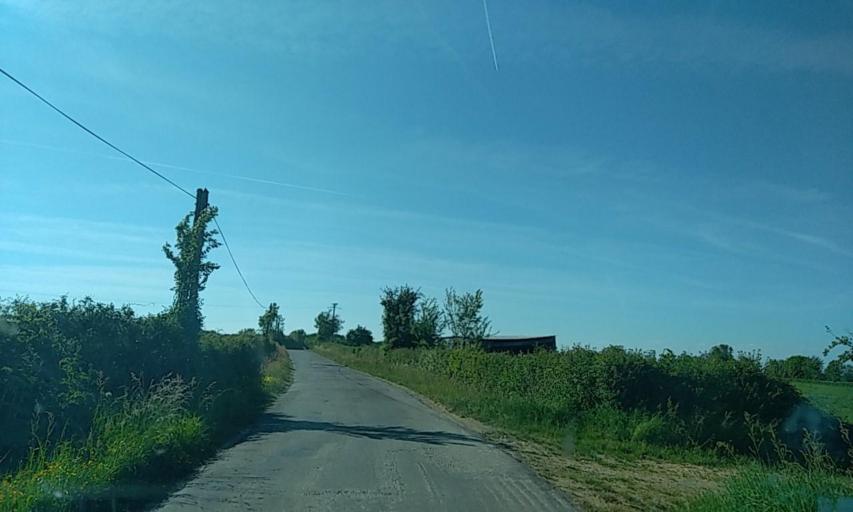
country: FR
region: Poitou-Charentes
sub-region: Departement des Deux-Sevres
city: Boisme
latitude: 46.7967
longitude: -0.4348
